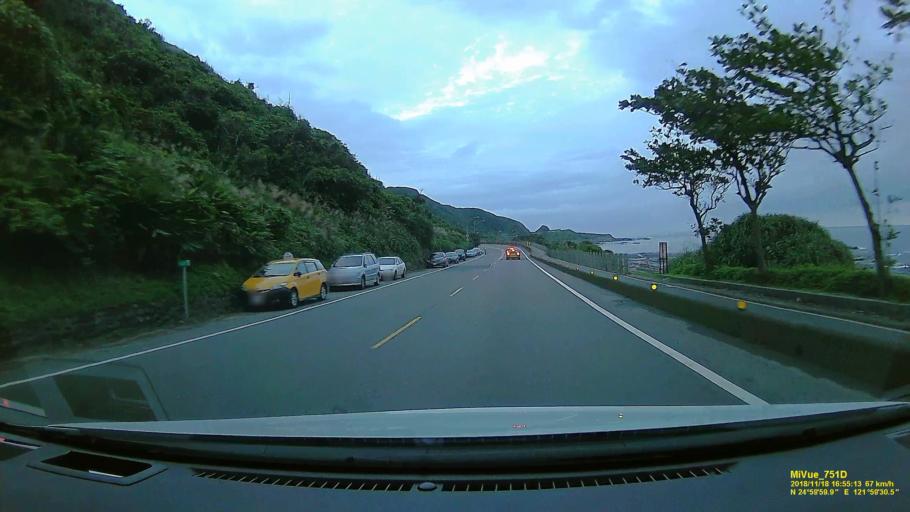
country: TW
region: Taiwan
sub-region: Keelung
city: Keelung
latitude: 25.0001
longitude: 121.9921
